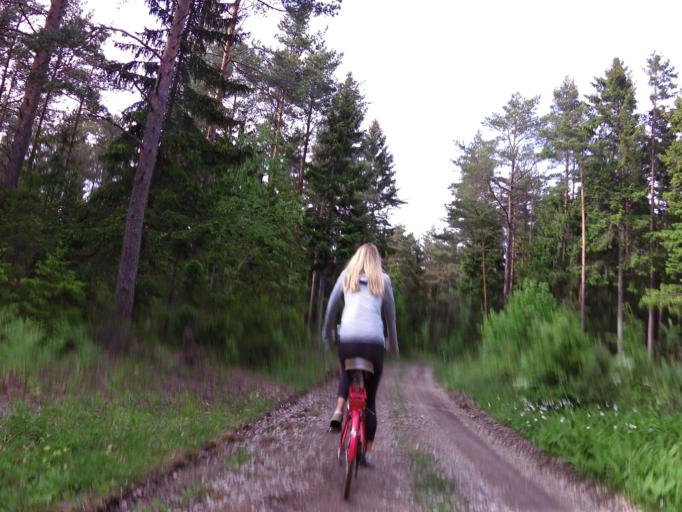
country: EE
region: Harju
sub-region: Paldiski linn
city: Paldiski
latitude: 59.2648
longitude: 23.7487
